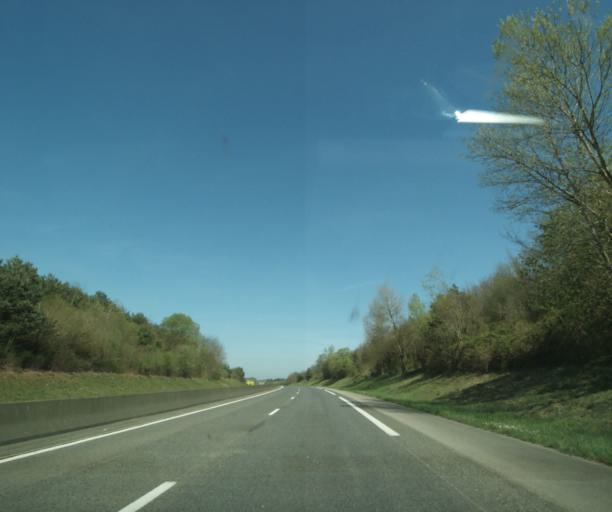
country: FR
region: Auvergne
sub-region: Departement de l'Allier
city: Yzeure
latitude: 46.5506
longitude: 3.3887
